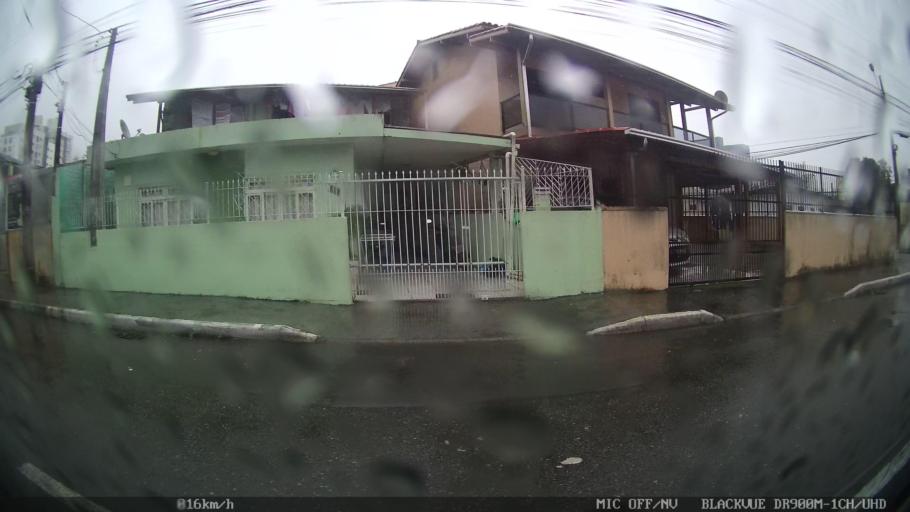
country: BR
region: Santa Catarina
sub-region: Itajai
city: Itajai
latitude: -26.9171
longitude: -48.6564
